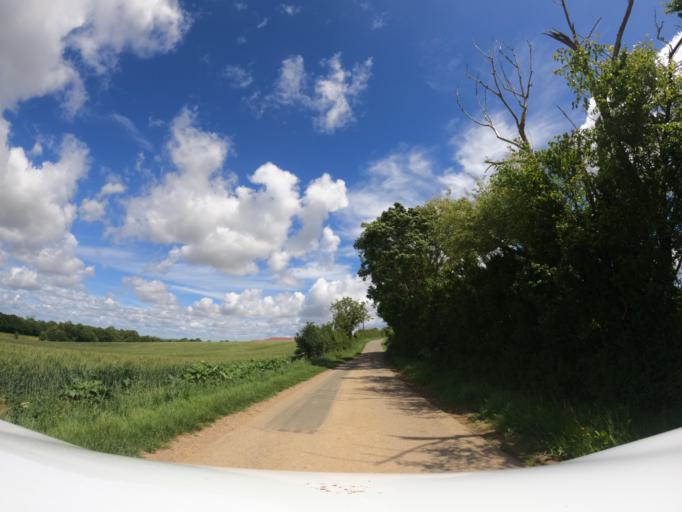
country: FR
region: Pays de la Loire
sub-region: Departement de la Vendee
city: Le Champ-Saint-Pere
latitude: 46.4766
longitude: -1.3127
